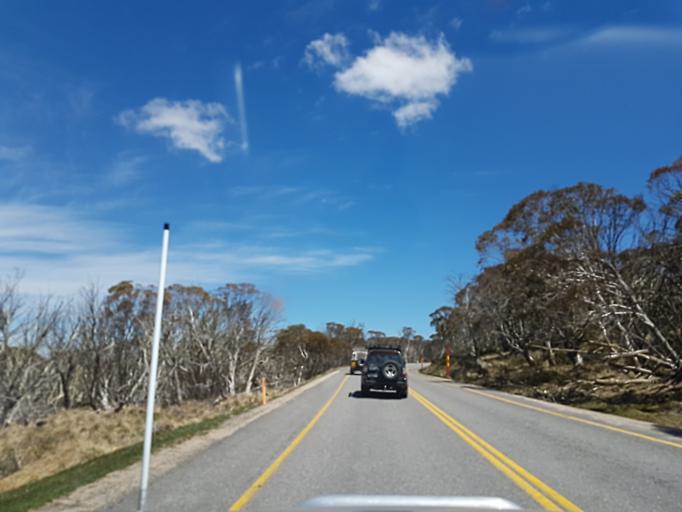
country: AU
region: Victoria
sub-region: Alpine
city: Mount Beauty
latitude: -37.0214
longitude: 147.2275
